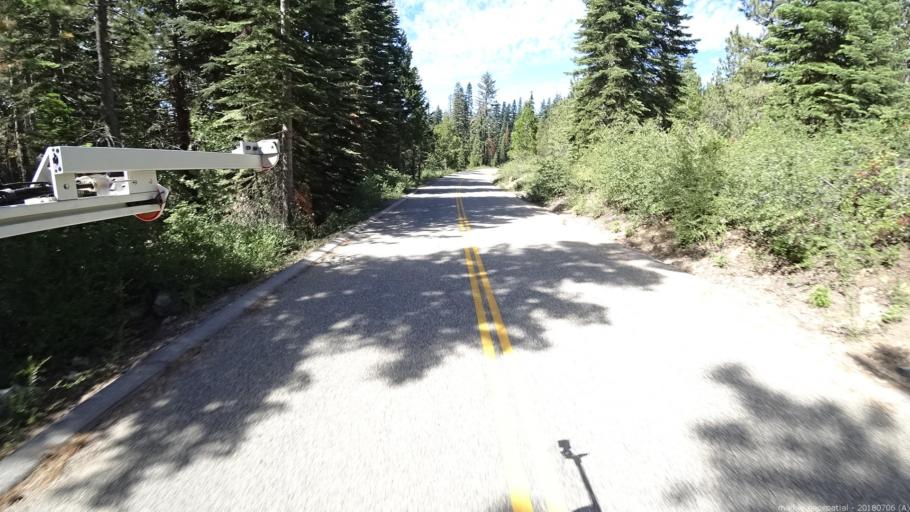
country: US
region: California
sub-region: Madera County
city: Oakhurst
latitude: 37.3975
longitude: -119.5170
